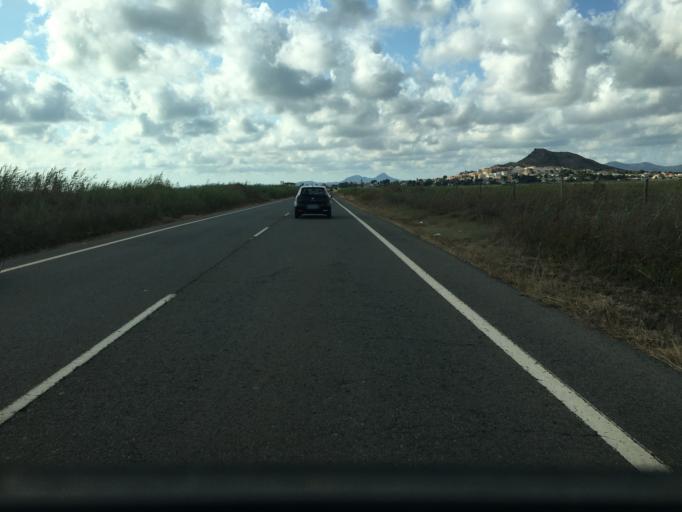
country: ES
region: Murcia
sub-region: Murcia
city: Los Alcazares
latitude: 37.7040
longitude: -0.8494
